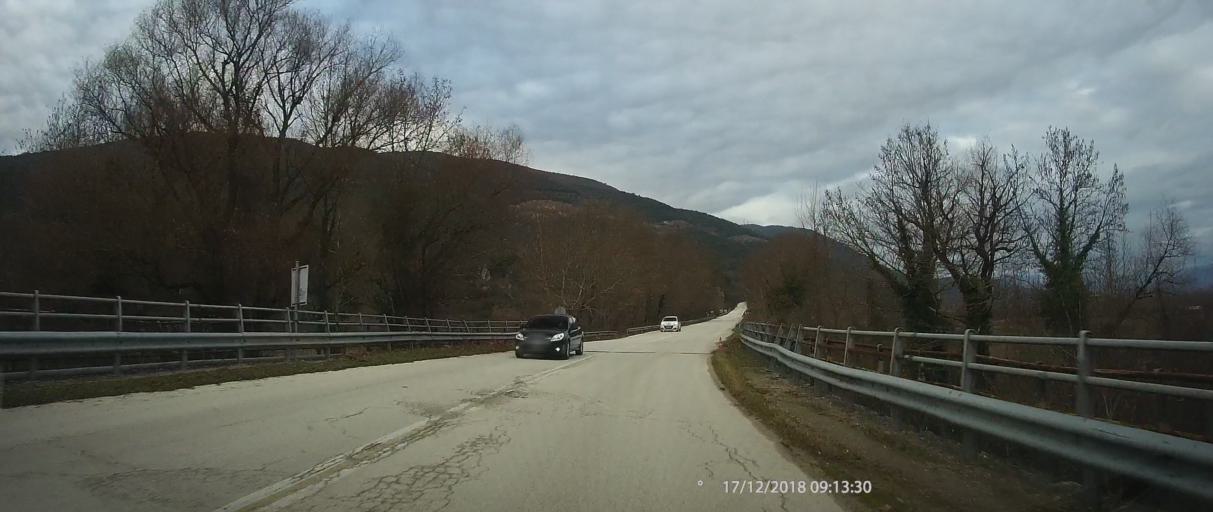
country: GR
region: Epirus
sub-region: Nomos Ioanninon
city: Kalpaki
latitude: 39.9732
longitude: 20.6585
